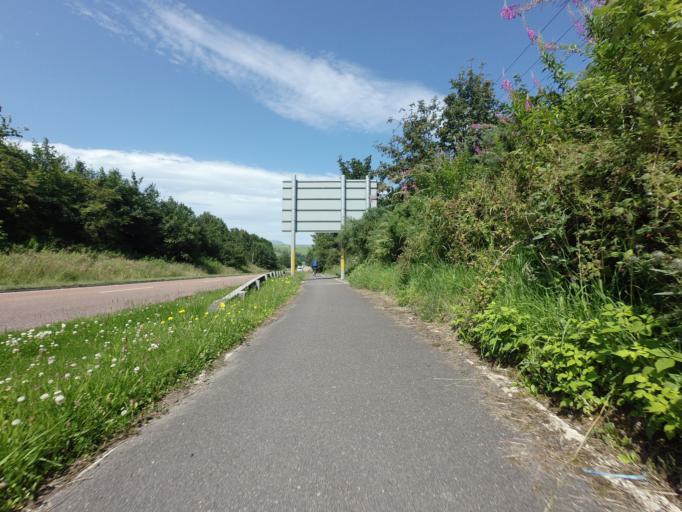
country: GB
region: Scotland
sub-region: Highland
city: Conon Bridge
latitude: 57.5690
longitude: -4.4261
